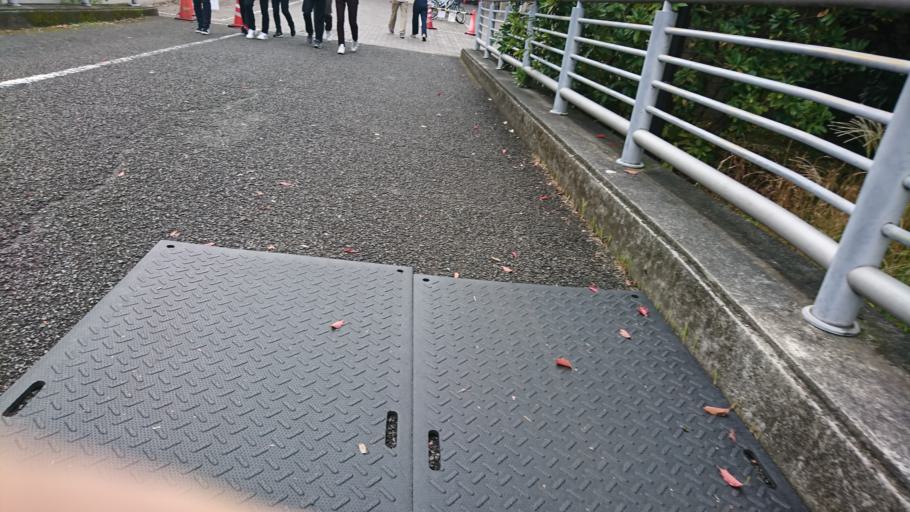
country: JP
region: Tokyo
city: Hino
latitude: 35.6175
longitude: 139.3783
